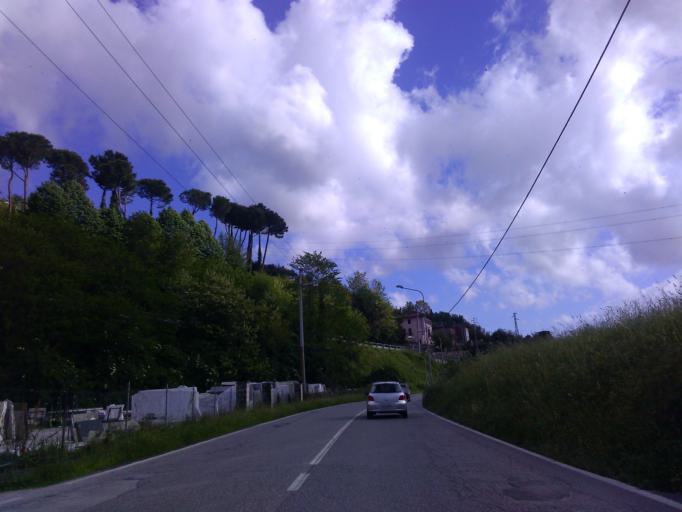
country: IT
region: Tuscany
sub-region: Provincia di Lucca
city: Ripa-Pozzi-Querceta-Ponterosso
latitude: 43.9784
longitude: 10.2210
